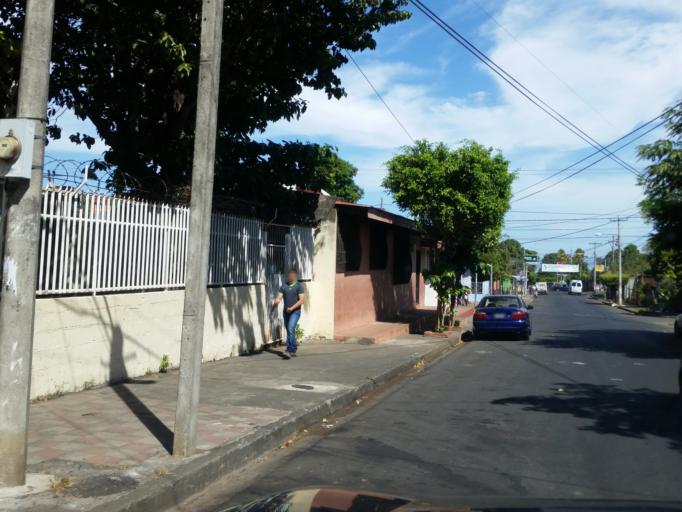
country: NI
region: Managua
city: Managua
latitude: 12.1367
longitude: -86.2918
